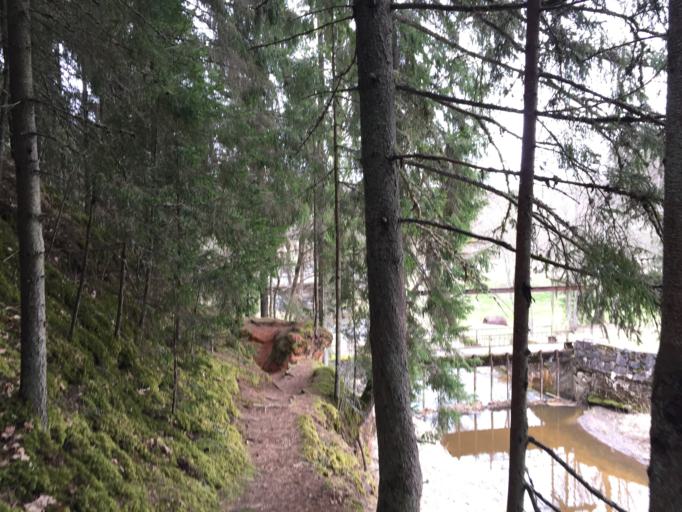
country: LV
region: Priekuli
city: Priekuli
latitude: 57.3301
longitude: 25.3920
